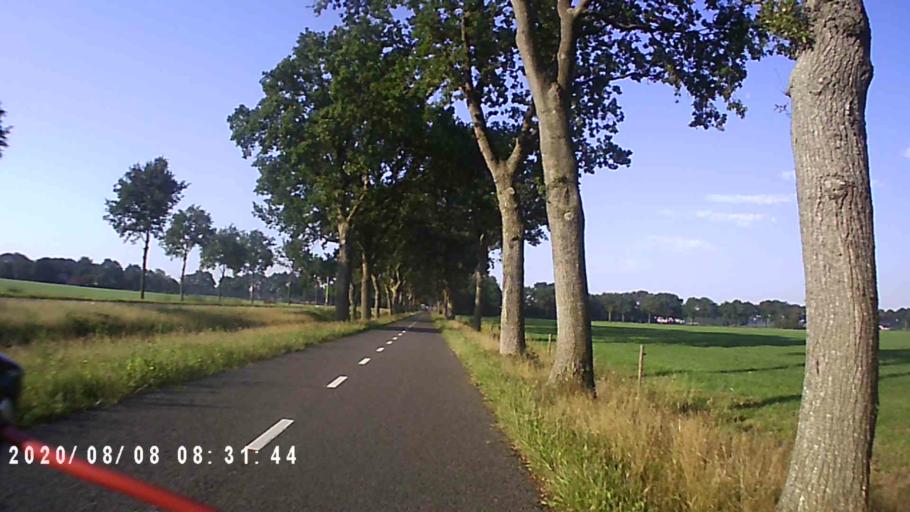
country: NL
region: Groningen
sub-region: Gemeente Leek
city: Leek
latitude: 53.0780
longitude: 6.3344
